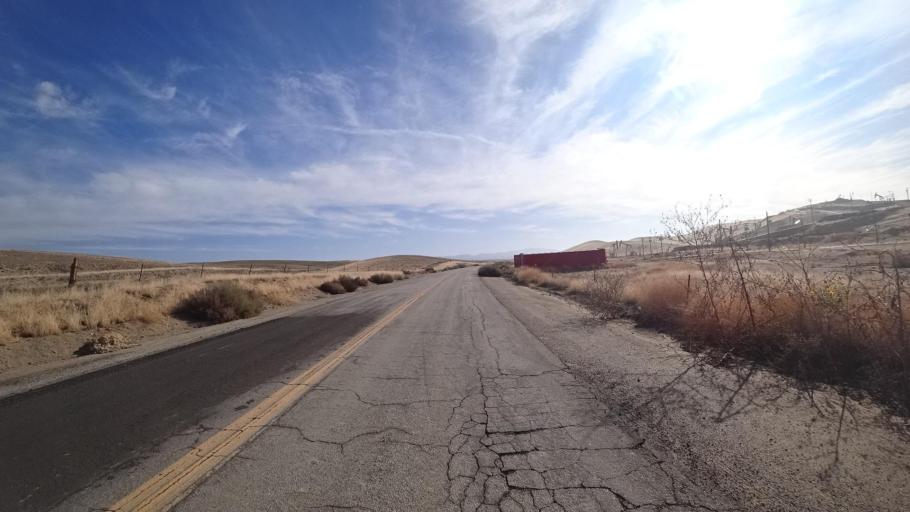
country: US
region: California
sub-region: Kern County
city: Oildale
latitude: 35.6114
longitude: -118.9707
